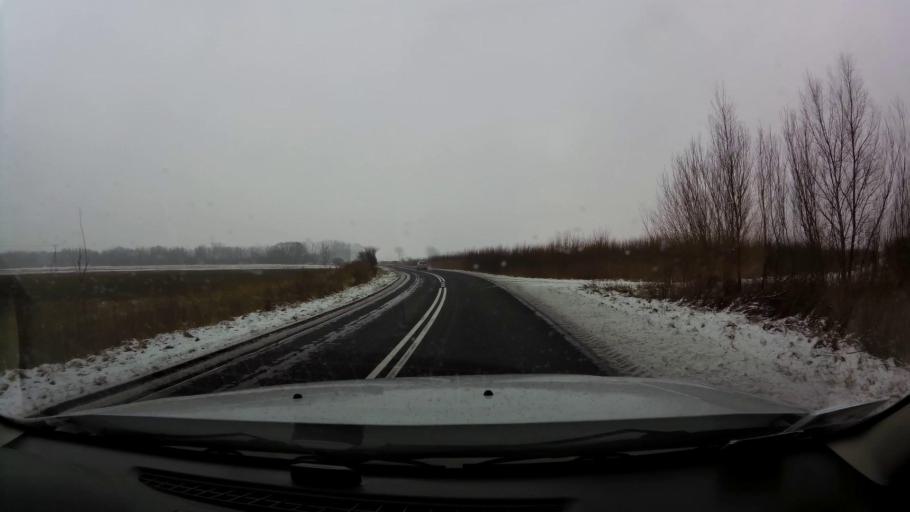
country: PL
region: West Pomeranian Voivodeship
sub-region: Powiat gryficki
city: Mrzezyno
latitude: 54.1111
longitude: 15.2654
